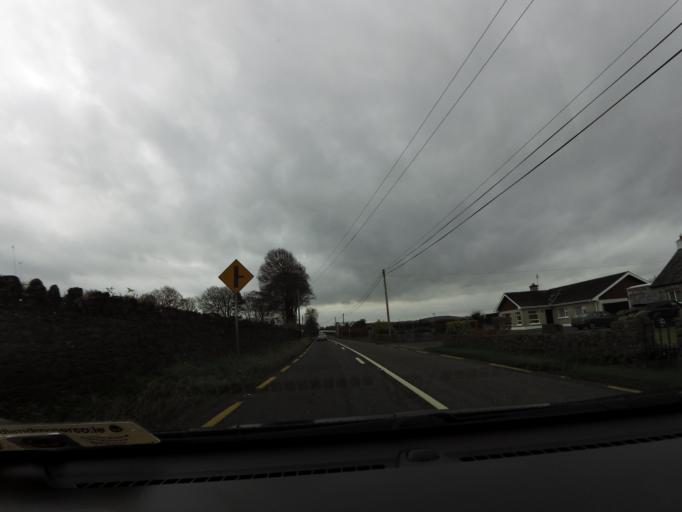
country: IE
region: Leinster
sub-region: Kilkenny
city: Ballyragget
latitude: 52.7378
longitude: -7.3195
